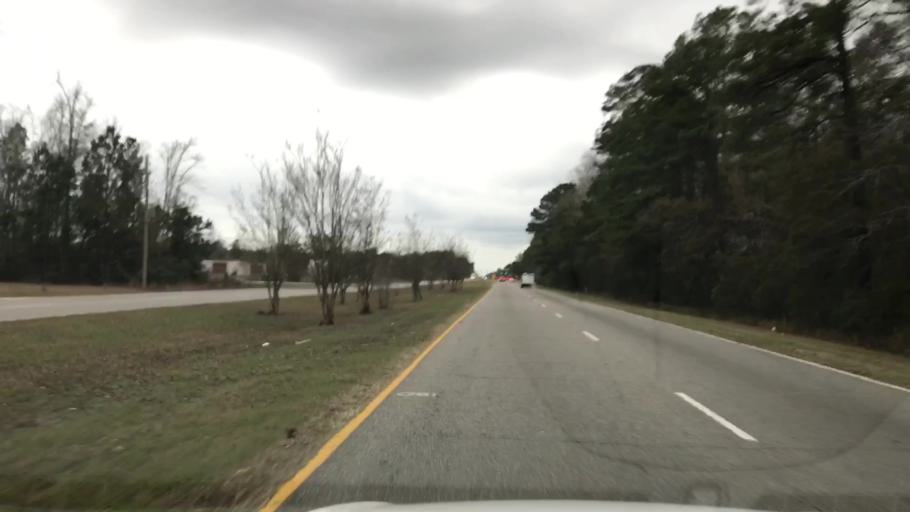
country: US
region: South Carolina
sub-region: Georgetown County
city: Georgetown
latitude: 33.3320
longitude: -79.3111
